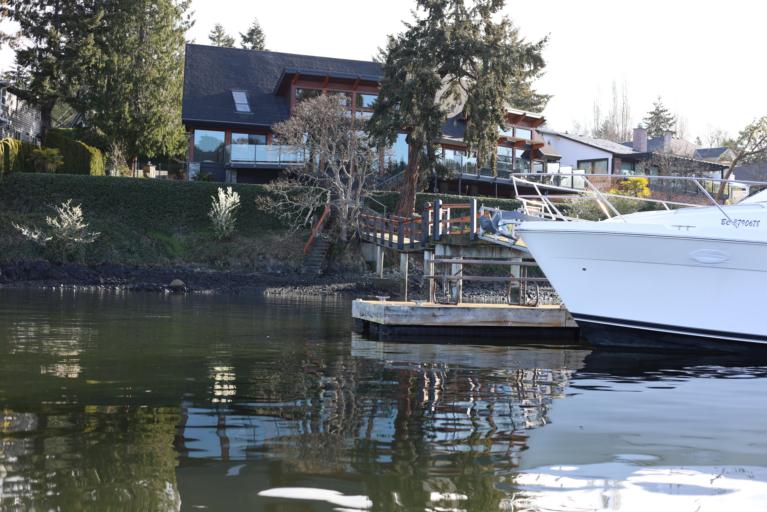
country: CA
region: British Columbia
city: North Saanich
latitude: 48.5739
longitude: -123.4652
